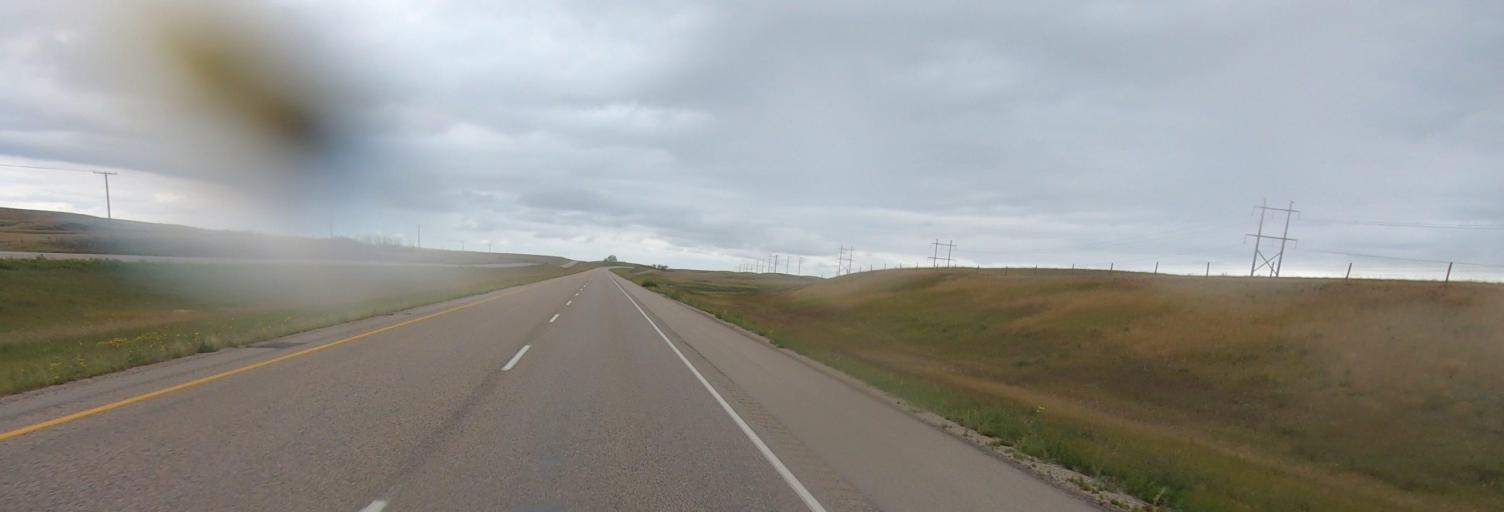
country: CA
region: Saskatchewan
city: Gravelbourg
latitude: 50.4631
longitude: -106.4254
